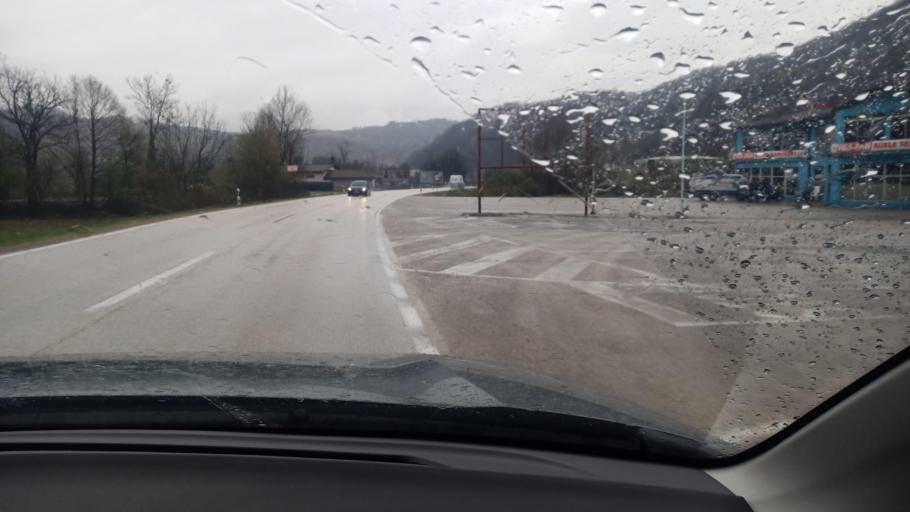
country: BA
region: Federation of Bosnia and Herzegovina
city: Bosanska Krupa
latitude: 44.9126
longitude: 16.1569
